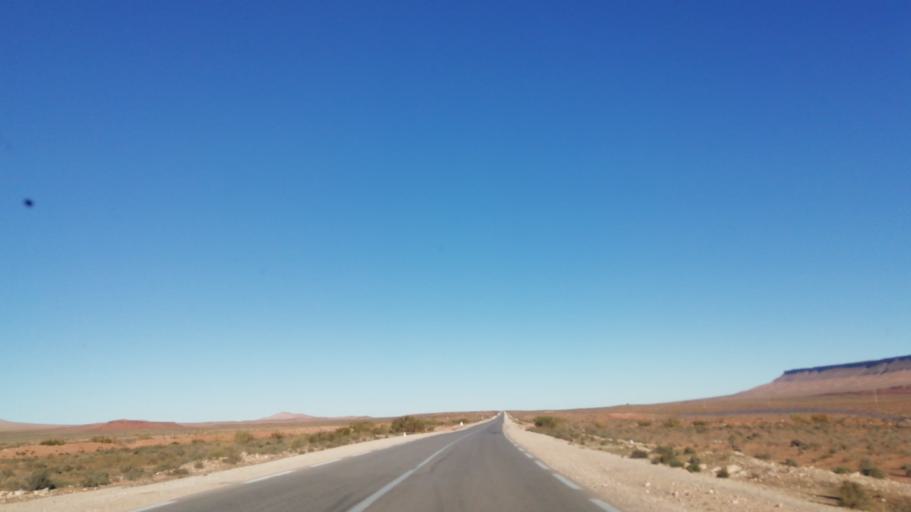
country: DZ
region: El Bayadh
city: El Abiodh Sidi Cheikh
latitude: 33.0863
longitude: 0.1811
